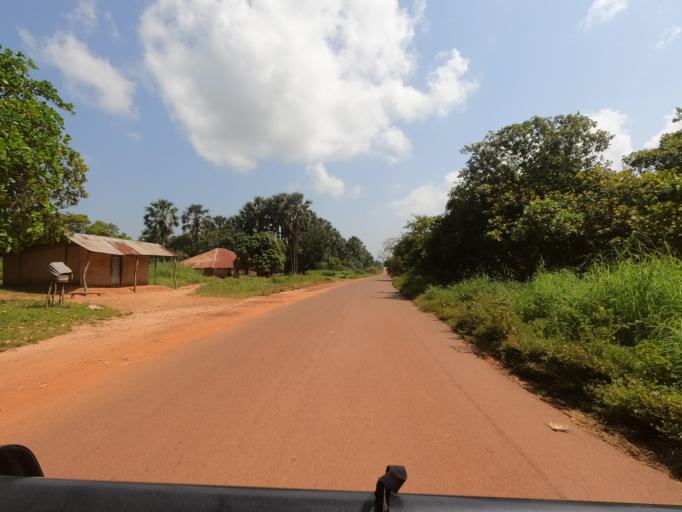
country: GW
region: Cacheu
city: Canchungo
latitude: 12.2845
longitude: -15.7828
